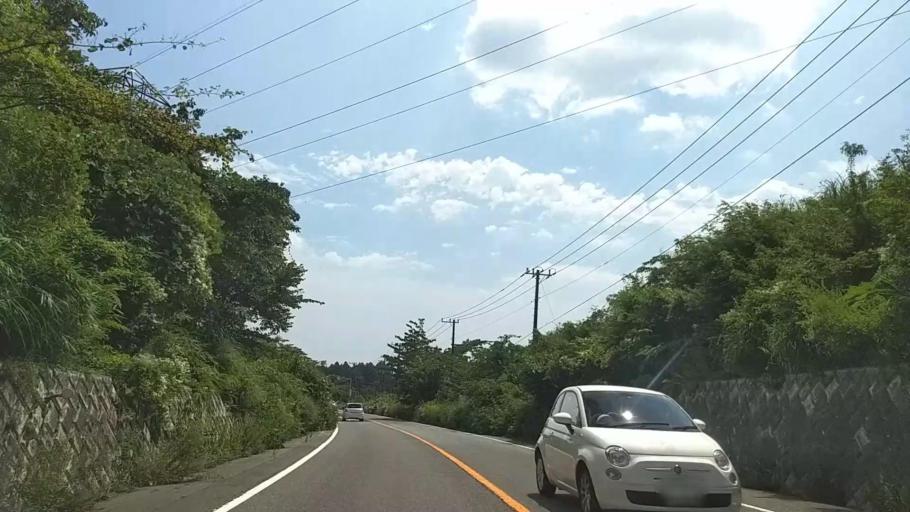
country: JP
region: Shizuoka
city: Fujinomiya
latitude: 35.3440
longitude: 138.5875
